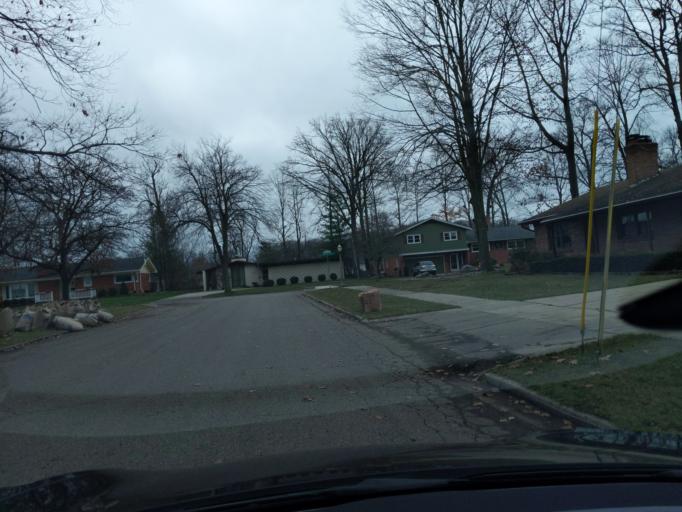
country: US
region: Michigan
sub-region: Ingham County
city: Edgemont Park
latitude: 42.7079
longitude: -84.5874
